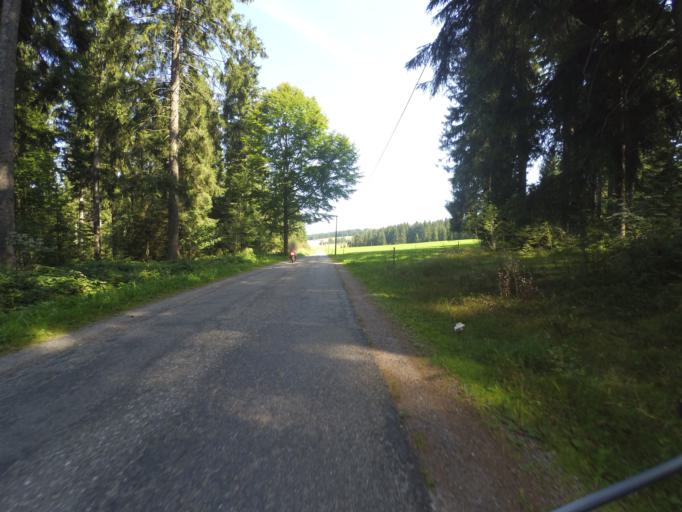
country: DE
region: Baden-Wuerttemberg
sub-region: Freiburg Region
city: Sankt Margen
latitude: 47.9667
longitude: 8.1214
